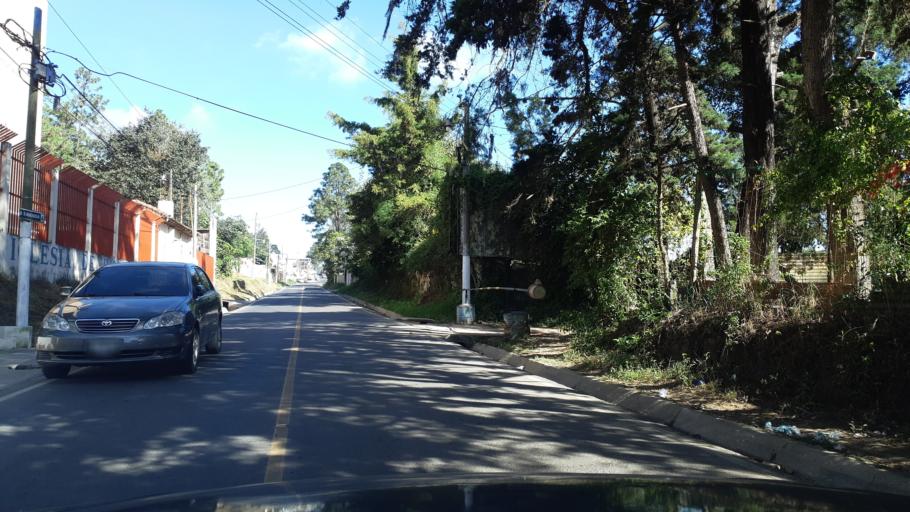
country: GT
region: Chimaltenango
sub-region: Municipio de Chimaltenango
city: Chimaltenango
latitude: 14.6494
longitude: -90.8204
